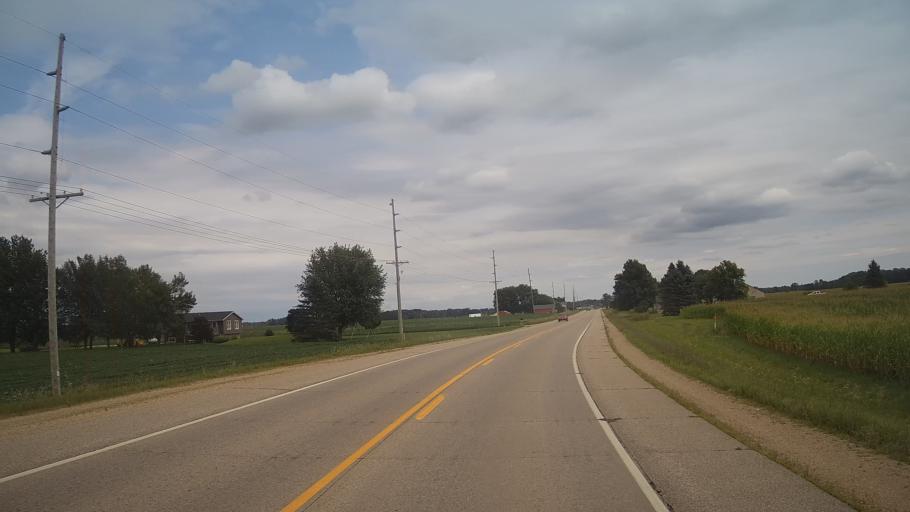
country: US
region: Wisconsin
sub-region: Waushara County
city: Redgranite
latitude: 44.0412
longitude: -89.0400
